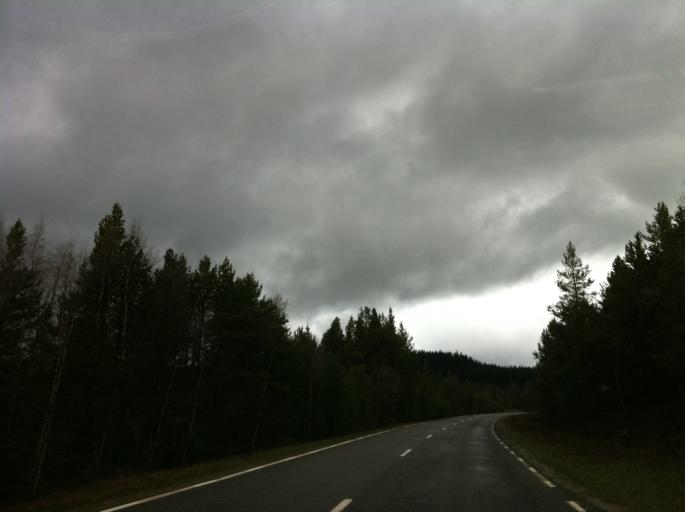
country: NO
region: Hedmark
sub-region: Engerdal
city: Engerdal
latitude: 62.4245
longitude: 12.7386
